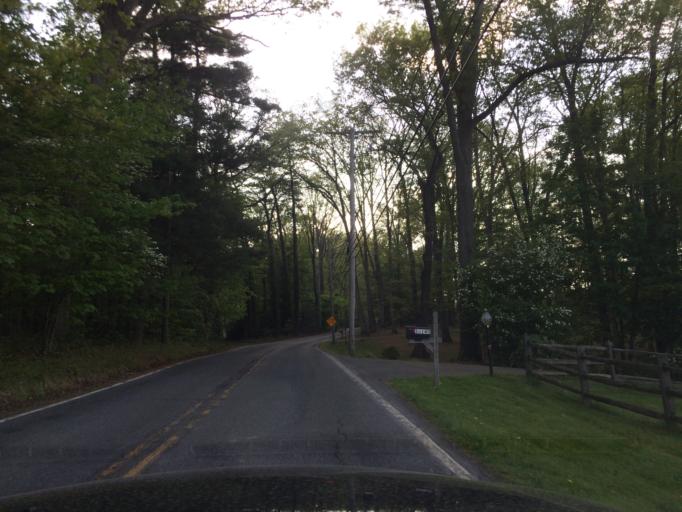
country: US
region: Maryland
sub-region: Carroll County
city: Mount Airy
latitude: 39.2936
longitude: -77.0762
